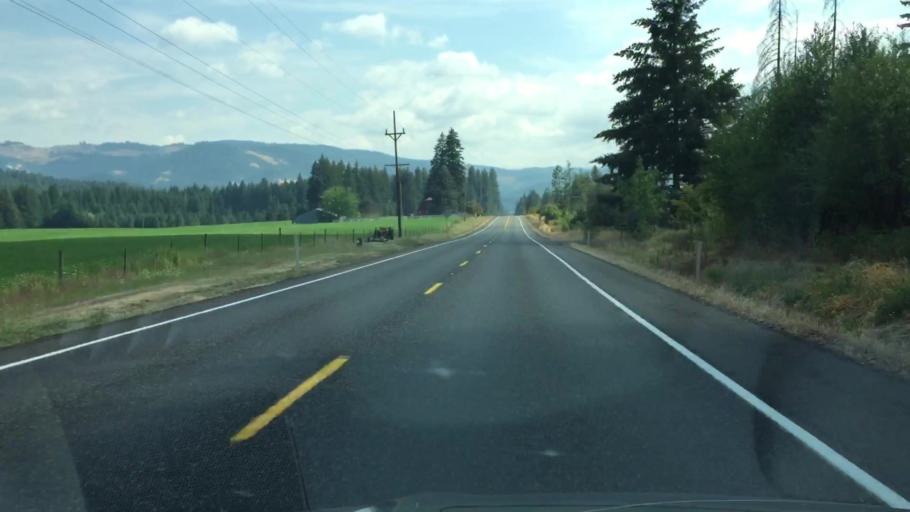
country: US
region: Washington
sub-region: Klickitat County
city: White Salmon
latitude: 45.8447
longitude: -121.5054
